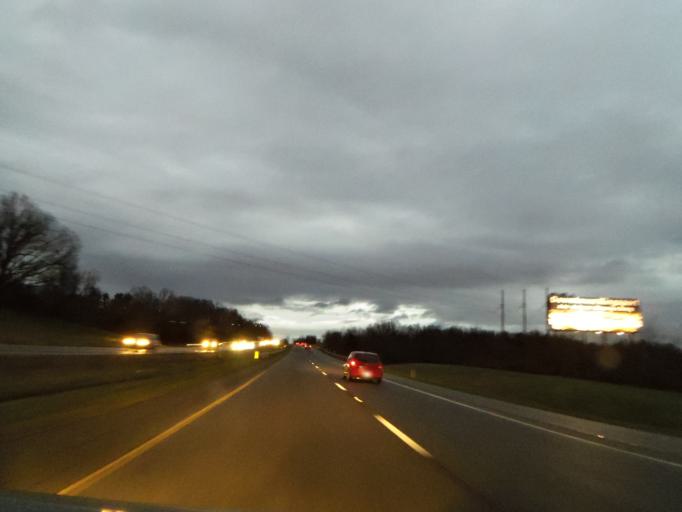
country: US
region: Tennessee
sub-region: Washington County
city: Gray
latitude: 36.4133
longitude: -82.4867
